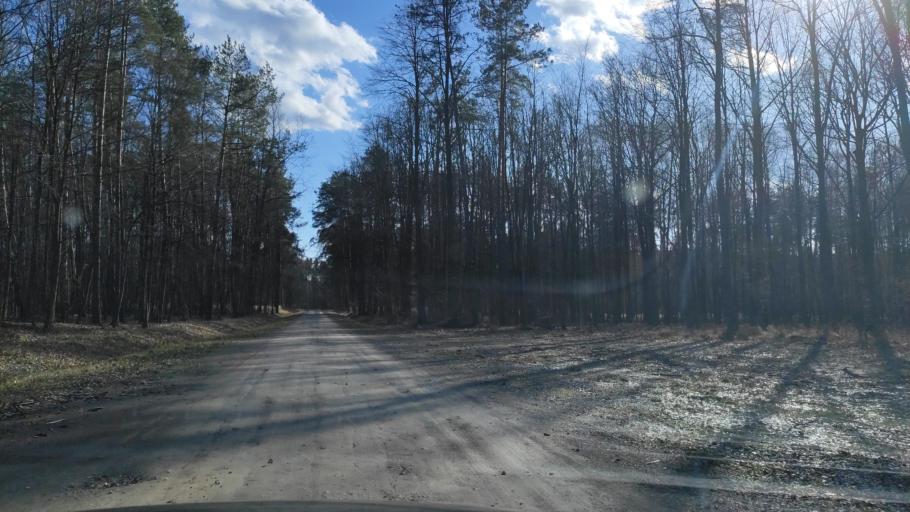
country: PL
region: Masovian Voivodeship
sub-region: Powiat radomski
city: Jedlnia-Letnisko
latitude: 51.4454
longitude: 21.2935
